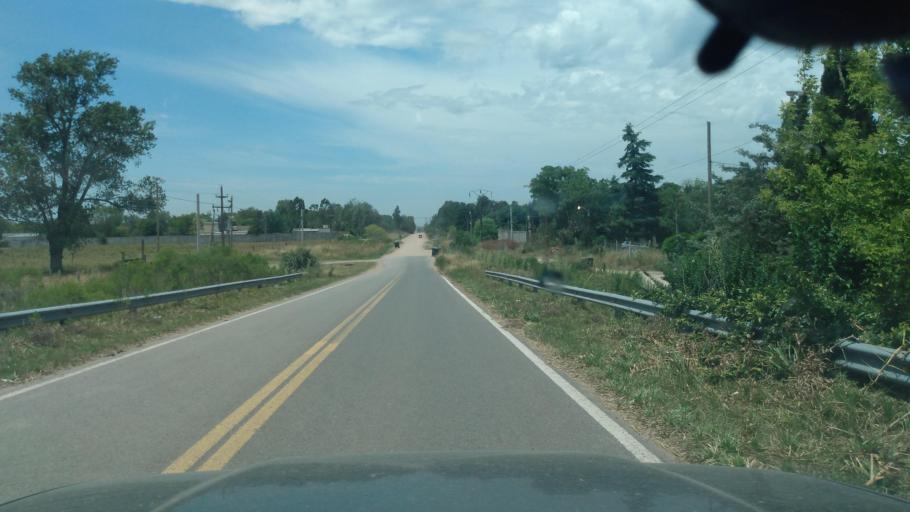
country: AR
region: Buenos Aires
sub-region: Partido de Lujan
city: Lujan
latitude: -34.5434
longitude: -59.1412
